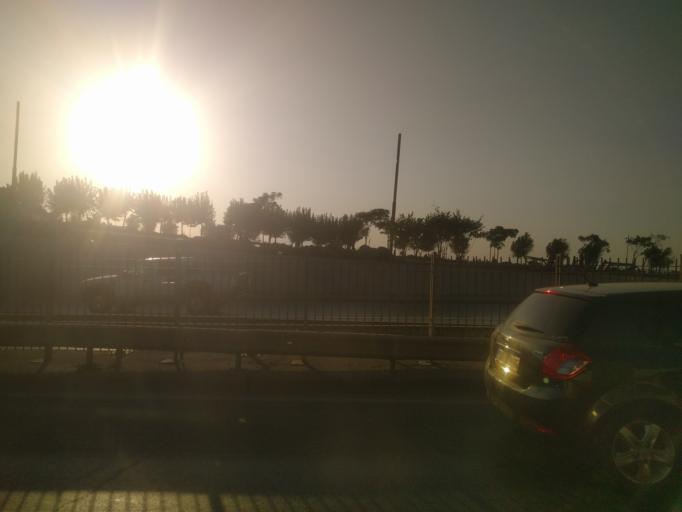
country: TR
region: Izmir
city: Izmir
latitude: 38.4193
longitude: 27.1280
